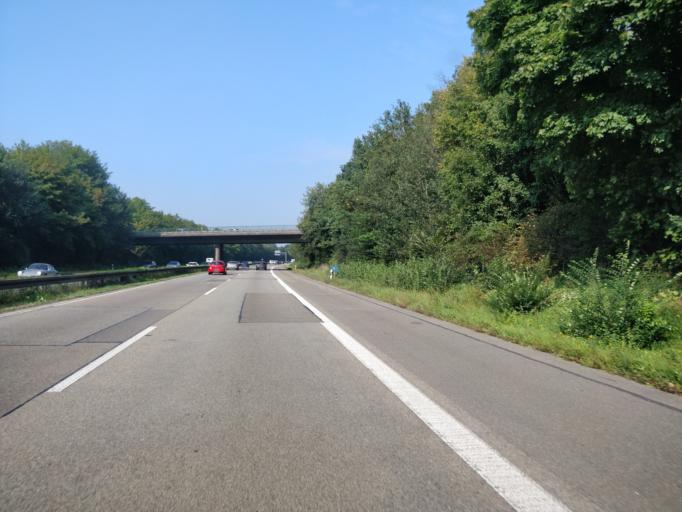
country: DE
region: North Rhine-Westphalia
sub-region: Regierungsbezirk Koln
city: Wahn-Heide
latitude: 50.8247
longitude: 7.1002
